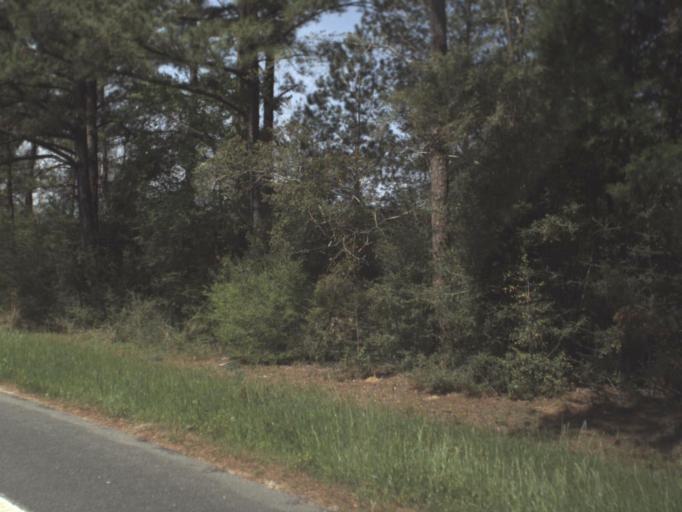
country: US
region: Florida
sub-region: Holmes County
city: Bonifay
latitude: 30.7606
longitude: -85.8742
